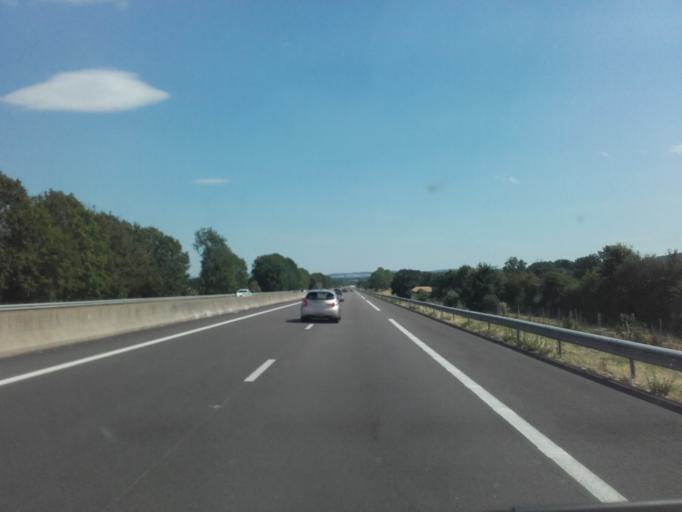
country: FR
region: Bourgogne
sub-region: Departement de la Cote-d'Or
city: Semur-en-Auxois
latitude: 47.4108
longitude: 4.3404
